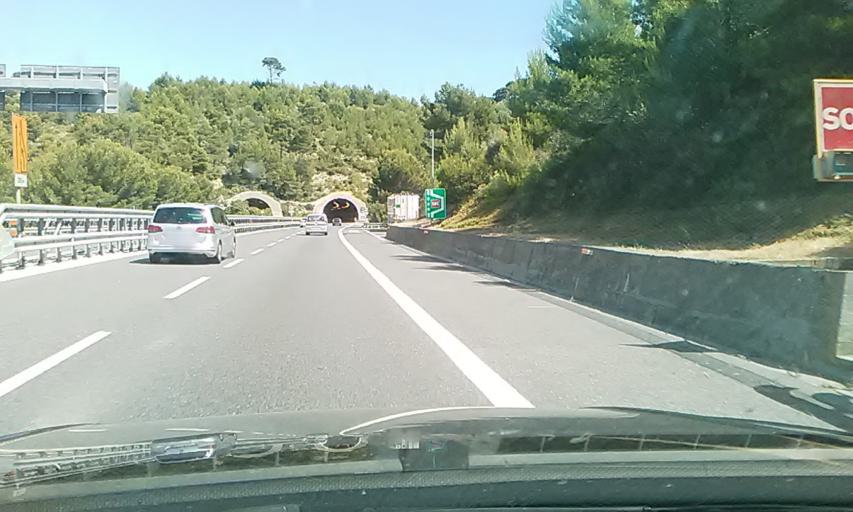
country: IT
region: Liguria
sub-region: Provincia di Savona
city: Laigueglia
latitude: 43.9759
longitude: 8.1410
